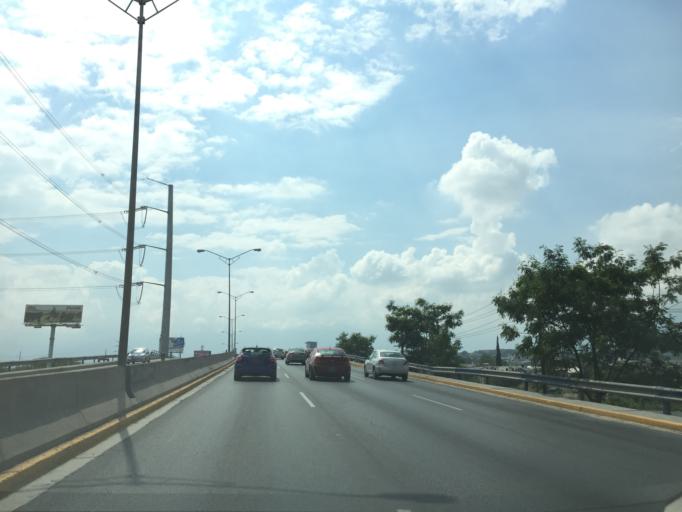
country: MX
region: Nuevo Leon
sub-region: San Nicolas de los Garza
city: San Nicolas de los Garza
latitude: 25.7536
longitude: -100.3083
